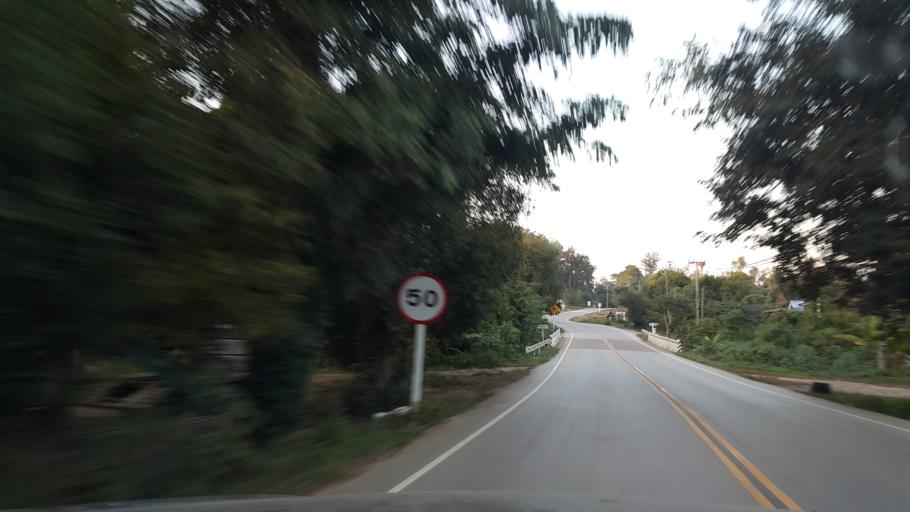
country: TH
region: Phrae
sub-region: Amphoe Wang Chin
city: Wang Chin
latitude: 17.8762
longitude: 99.6195
